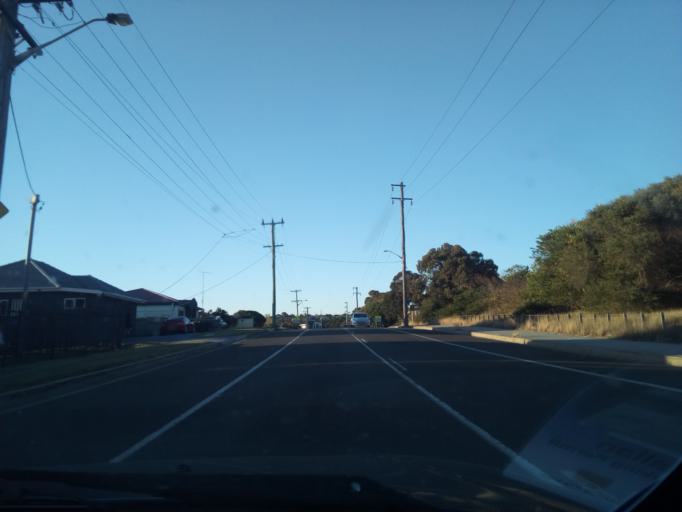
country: AU
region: New South Wales
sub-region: Wollongong
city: Port Kembla
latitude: -34.4923
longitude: 150.8934
